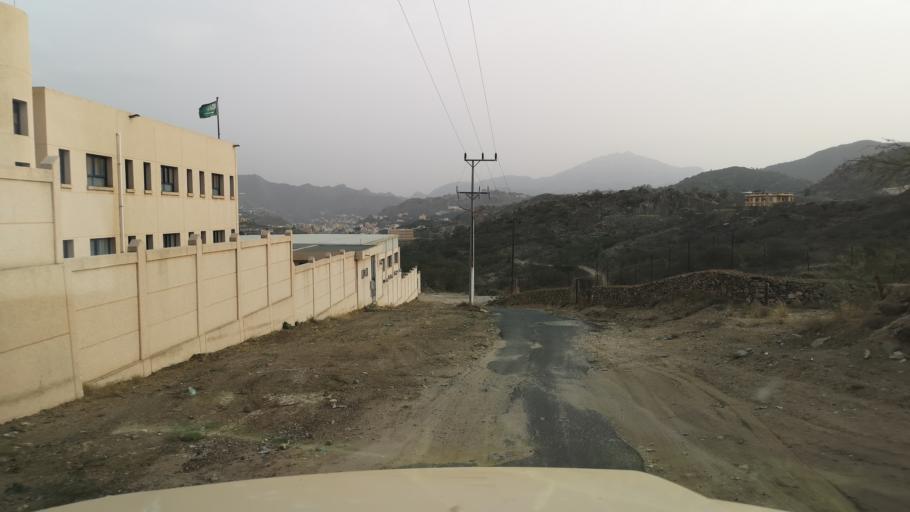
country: YE
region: Sa'dah
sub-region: Monabbih
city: Suq al Khamis
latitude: 17.3728
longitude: 43.1269
